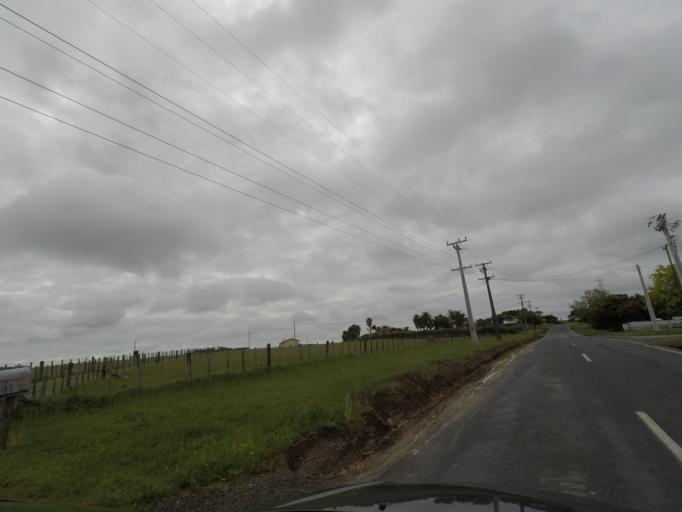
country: NZ
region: Auckland
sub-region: Auckland
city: Rosebank
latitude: -36.8093
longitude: 174.5770
